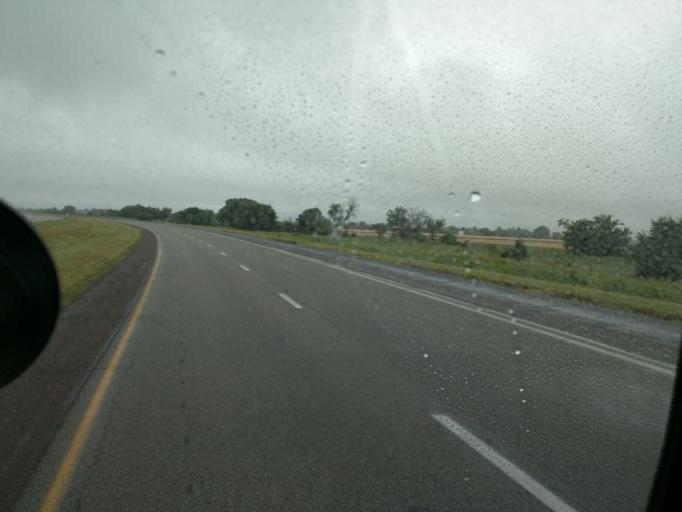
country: US
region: Kansas
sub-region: Reno County
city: South Hutchinson
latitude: 37.9475
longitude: -97.8872
